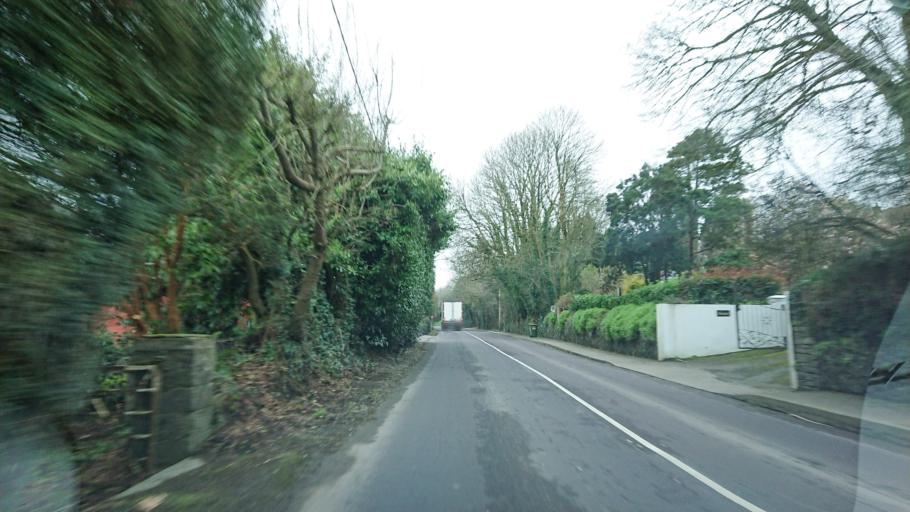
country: IE
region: Munster
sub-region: County Cork
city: Bandon
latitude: 51.7469
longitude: -8.7536
